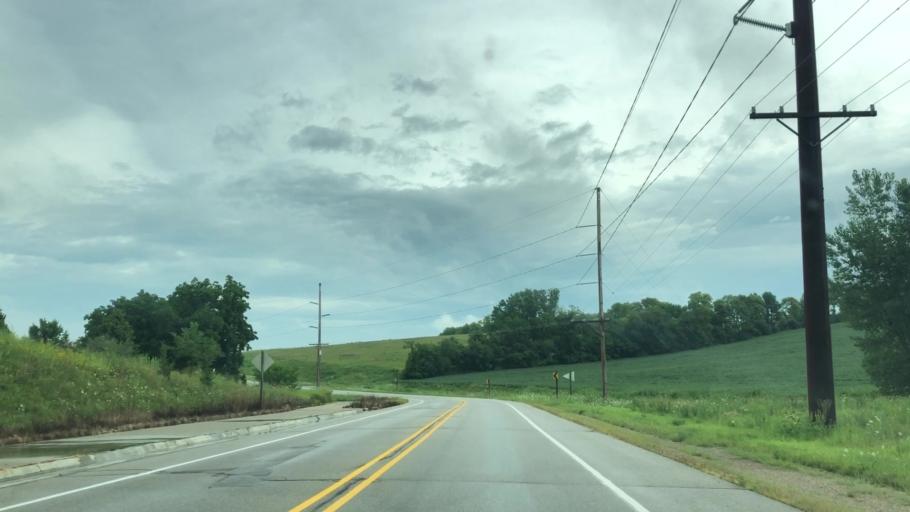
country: US
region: Iowa
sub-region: Marshall County
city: Marshalltown
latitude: 42.0086
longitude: -92.9610
